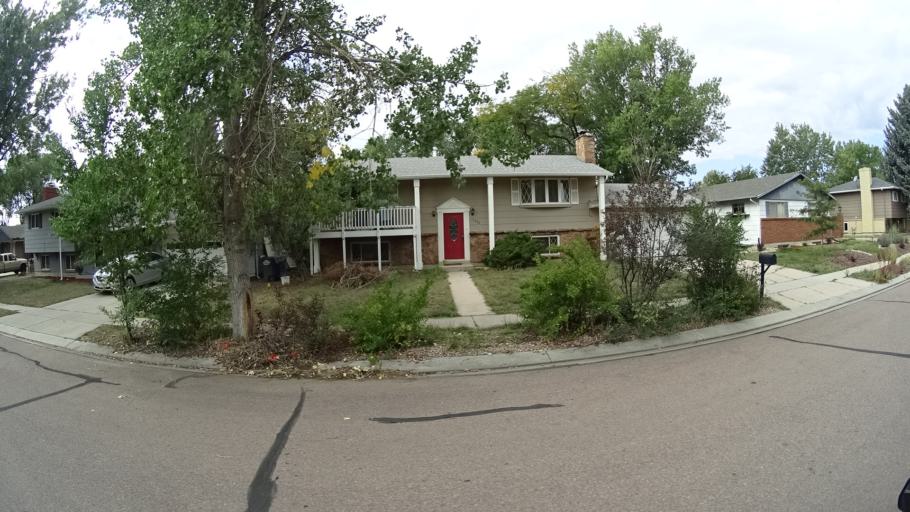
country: US
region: Colorado
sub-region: El Paso County
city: Cimarron Hills
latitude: 38.8508
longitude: -104.7459
